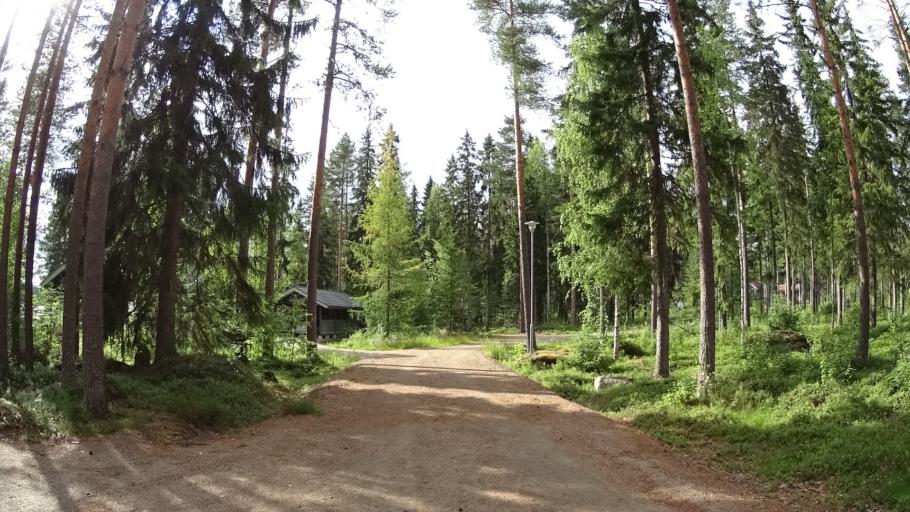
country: FI
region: Southern Ostrobothnia
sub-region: Kuusiokunnat
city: AEhtaeri
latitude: 62.5281
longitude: 24.1942
